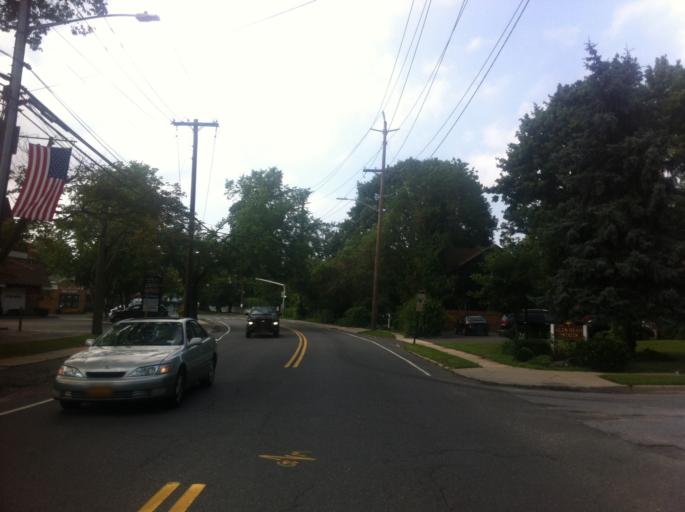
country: US
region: New York
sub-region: Nassau County
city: Glen Head
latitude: 40.8359
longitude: -73.6280
